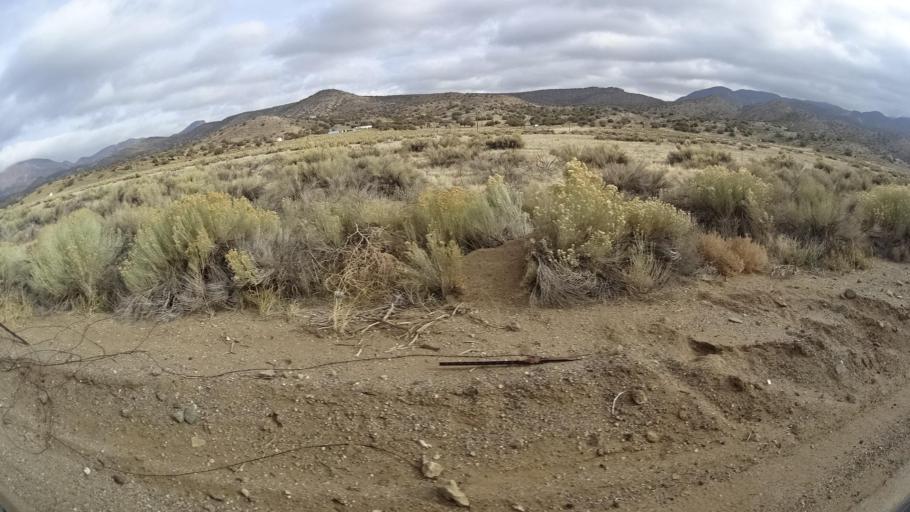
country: US
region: California
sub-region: Kern County
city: Tehachapi
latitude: 35.1585
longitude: -118.3234
